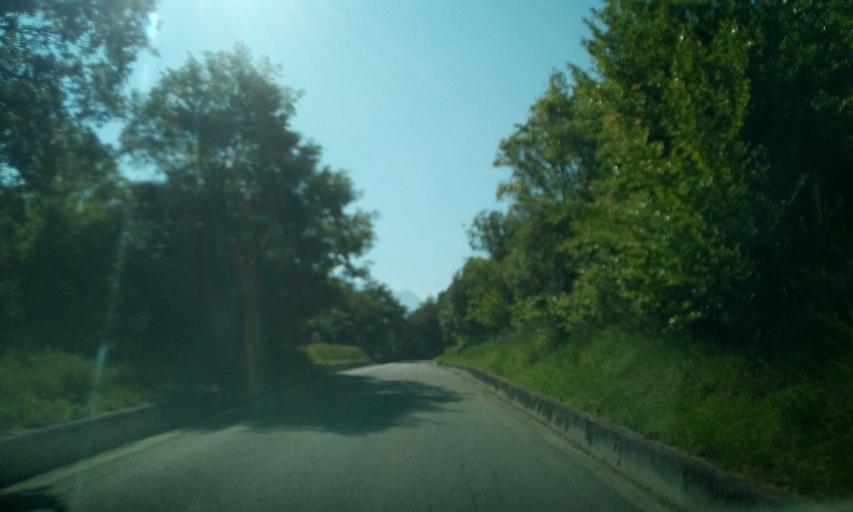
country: IT
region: Aosta Valley
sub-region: Valle d'Aosta
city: Chatillon
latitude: 45.7436
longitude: 7.6292
